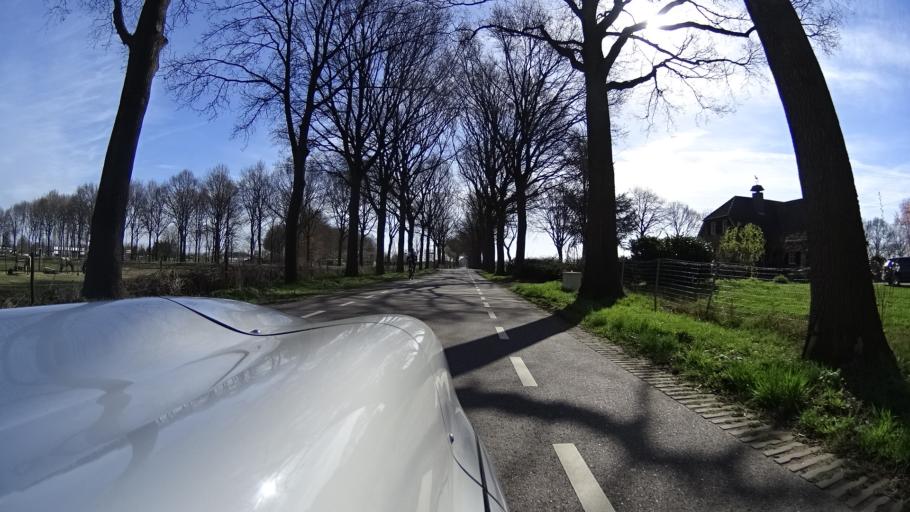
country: NL
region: North Brabant
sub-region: Gemeente Cuijk
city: Cuijk
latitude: 51.7174
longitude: 5.8269
